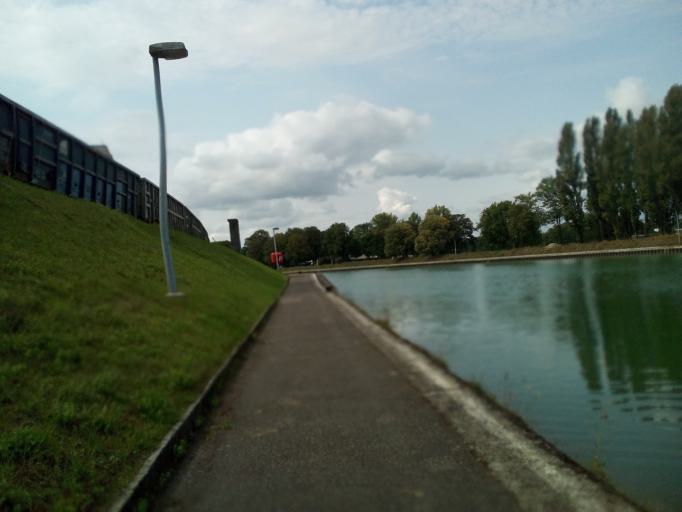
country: CH
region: Basel-Landschaft
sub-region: Bezirk Arlesheim
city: Birsfelden
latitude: 47.5581
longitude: 7.6369
